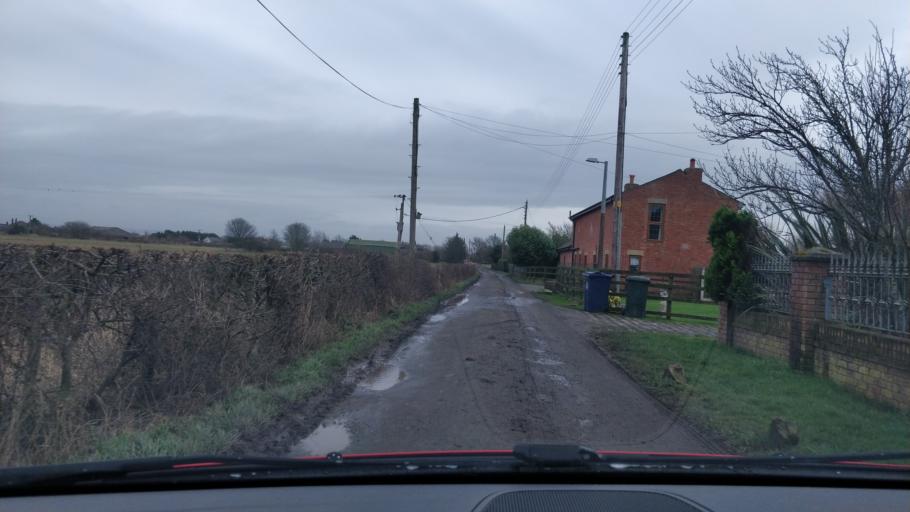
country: GB
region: England
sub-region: Lancashire
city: Banks
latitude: 53.6854
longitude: -2.9309
